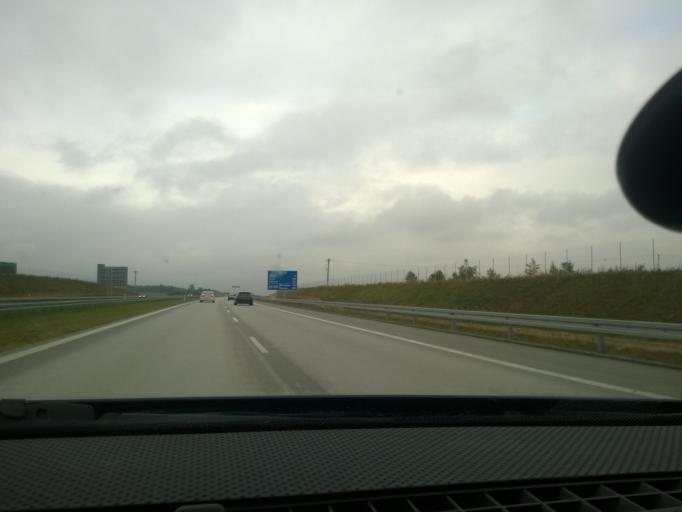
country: PL
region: Lodz Voivodeship
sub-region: Powiat lodzki wschodni
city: Andrespol
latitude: 51.8055
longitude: 19.6275
